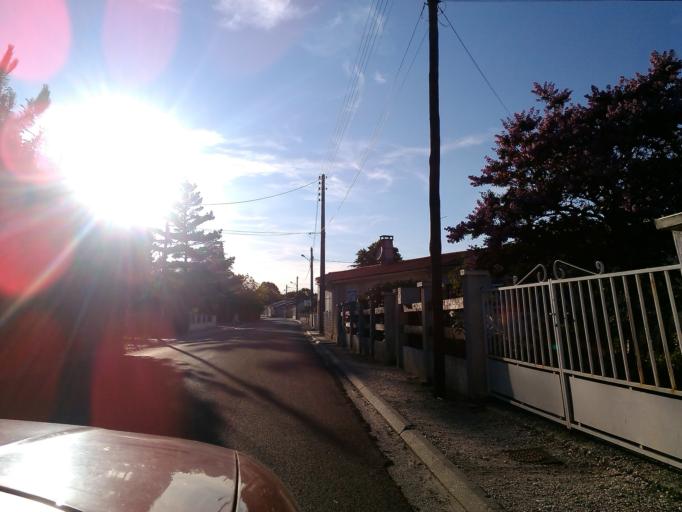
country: FR
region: Aquitaine
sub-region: Departement de la Gironde
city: Soulac-sur-Mer
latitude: 45.4301
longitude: -1.0322
